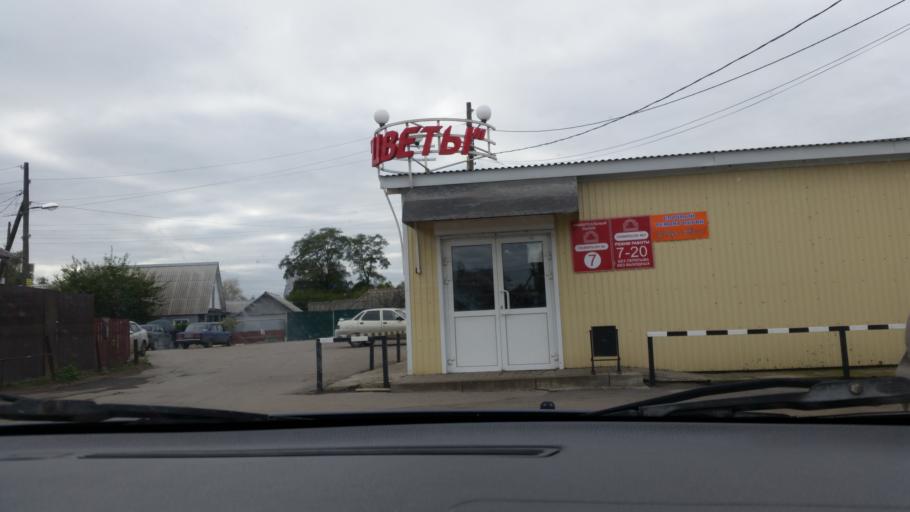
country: RU
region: Lipetsk
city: Gryazi
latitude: 52.4904
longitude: 39.9511
